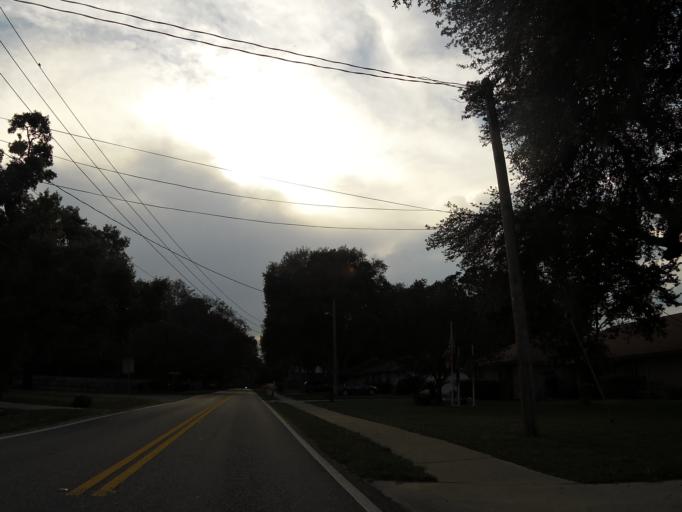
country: US
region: Florida
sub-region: Saint Johns County
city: Fruit Cove
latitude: 30.1390
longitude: -81.6003
